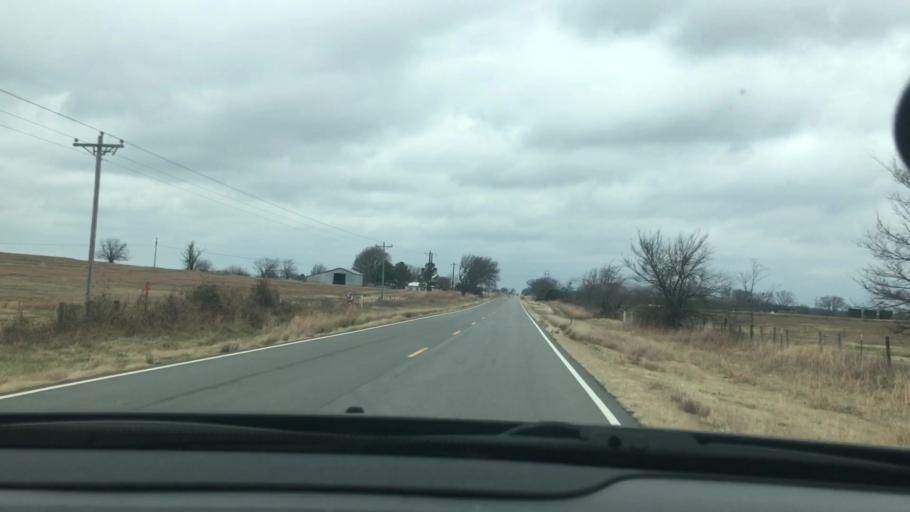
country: US
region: Oklahoma
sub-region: Atoka County
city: Atoka
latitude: 34.3750
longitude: -96.2274
